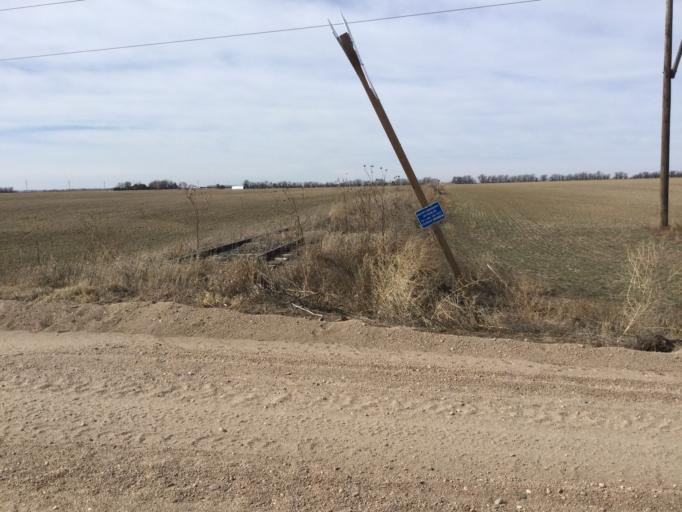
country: US
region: Kansas
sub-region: Rice County
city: Lyons
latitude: 38.3515
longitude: -98.2571
